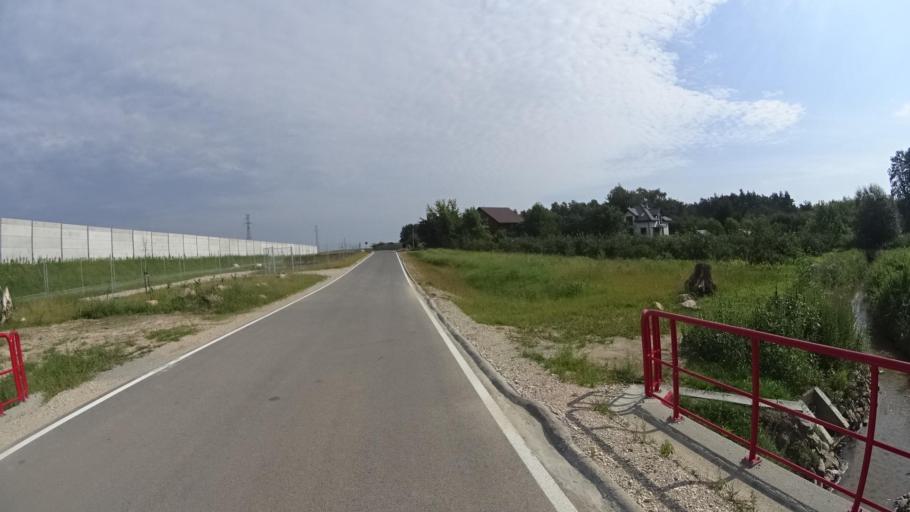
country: PL
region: Masovian Voivodeship
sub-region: Powiat piaseczynski
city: Tarczyn
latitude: 51.9616
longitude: 20.8564
